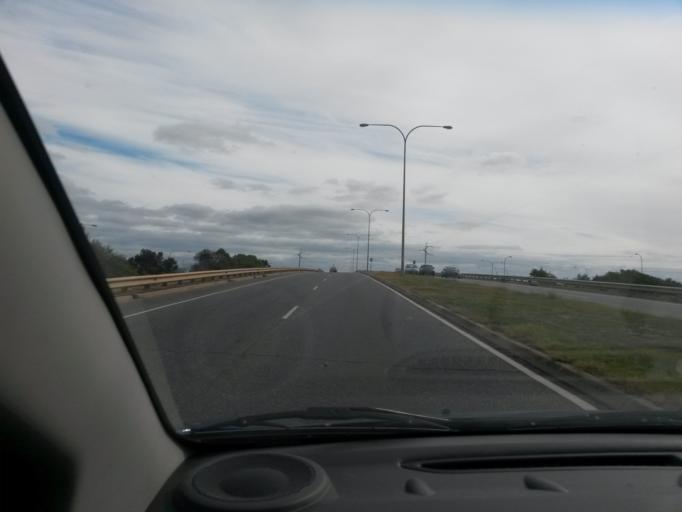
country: AU
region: South Australia
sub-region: Salisbury
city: Ingle Farm
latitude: -34.8101
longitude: 138.5988
